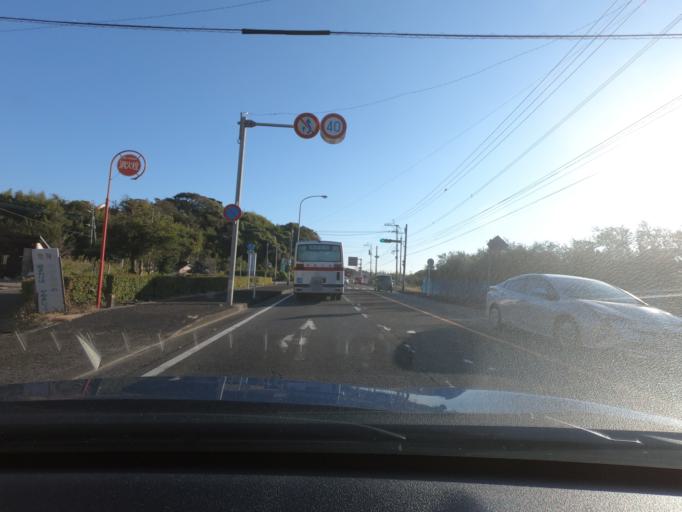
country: JP
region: Kagoshima
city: Akune
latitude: 31.9843
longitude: 130.2038
